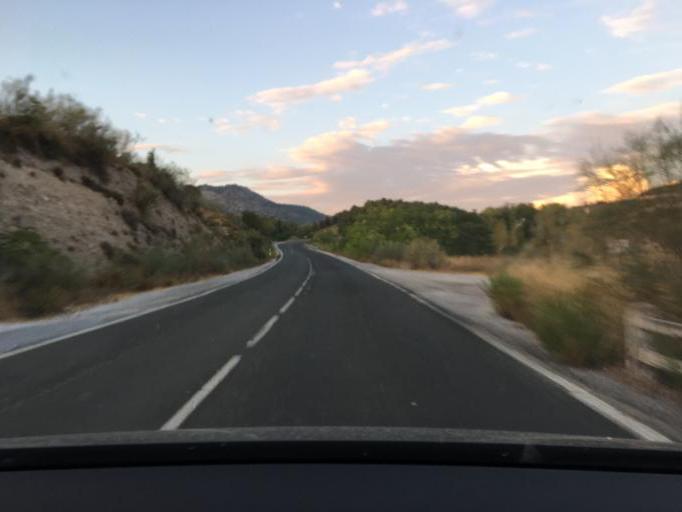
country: ES
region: Andalusia
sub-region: Provincia de Granada
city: Viznar
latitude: 37.2166
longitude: -3.5443
